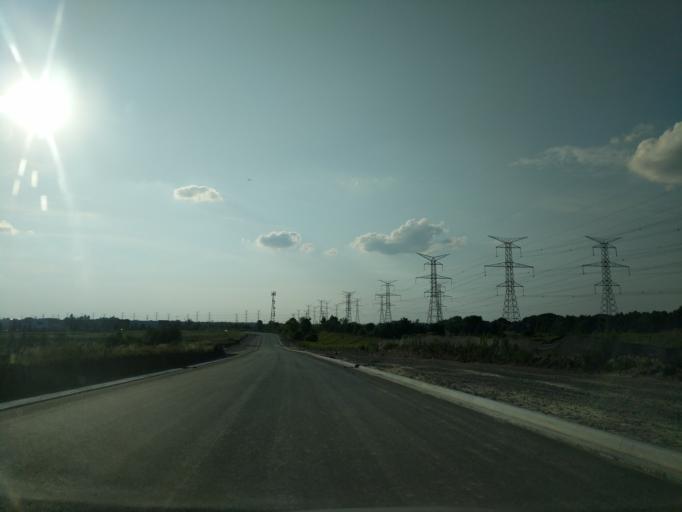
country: CA
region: Ontario
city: Markham
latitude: 43.8507
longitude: -79.2439
